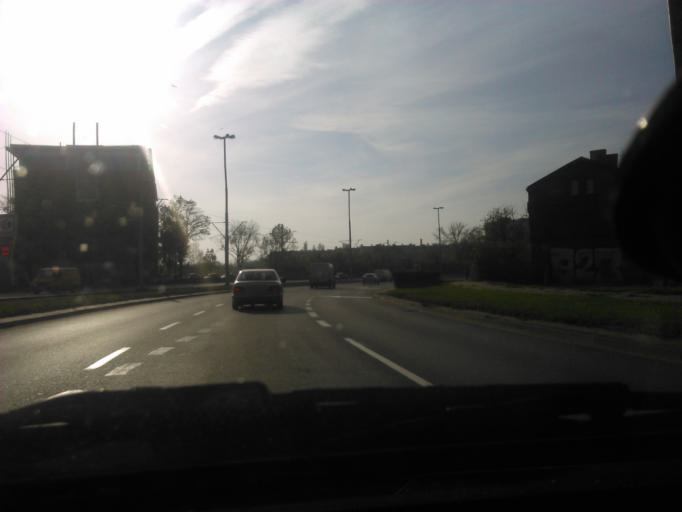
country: PL
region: Pomeranian Voivodeship
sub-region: Gdansk
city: Gdansk
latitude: 54.3462
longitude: 18.6684
